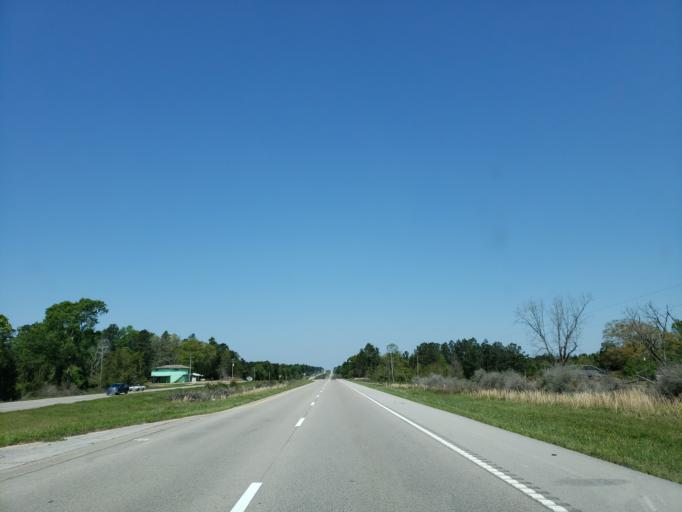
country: US
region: Mississippi
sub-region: Stone County
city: Wiggins
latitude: 30.9191
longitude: -89.1745
